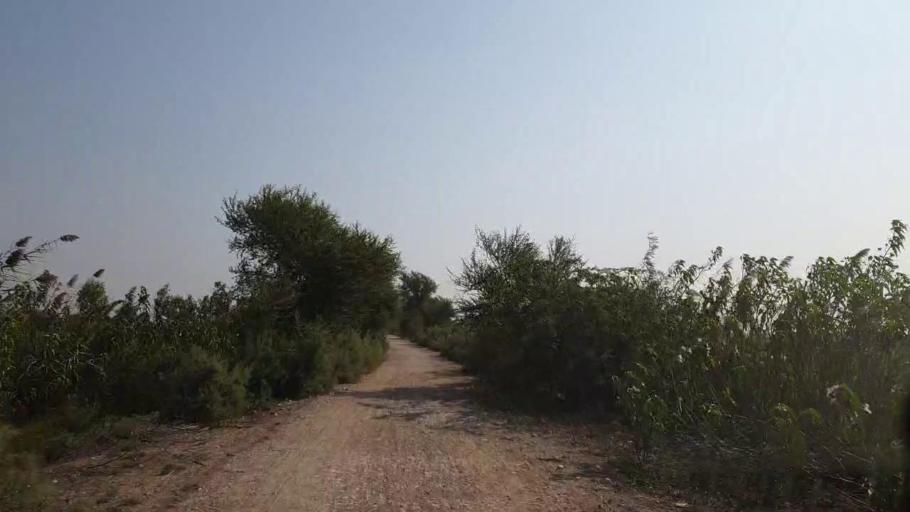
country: PK
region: Sindh
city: Tando Muhammad Khan
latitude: 25.0695
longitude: 68.4221
